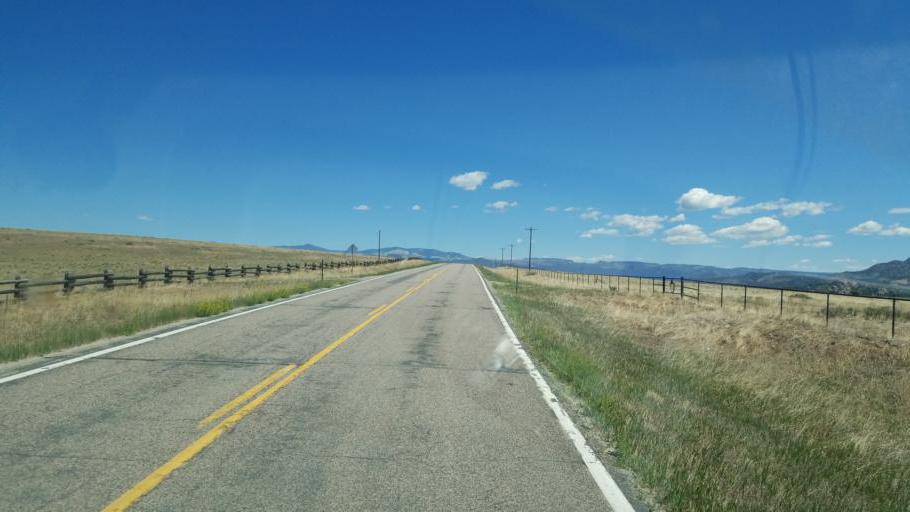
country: US
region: Colorado
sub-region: Custer County
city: Westcliffe
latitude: 38.2771
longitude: -105.6162
